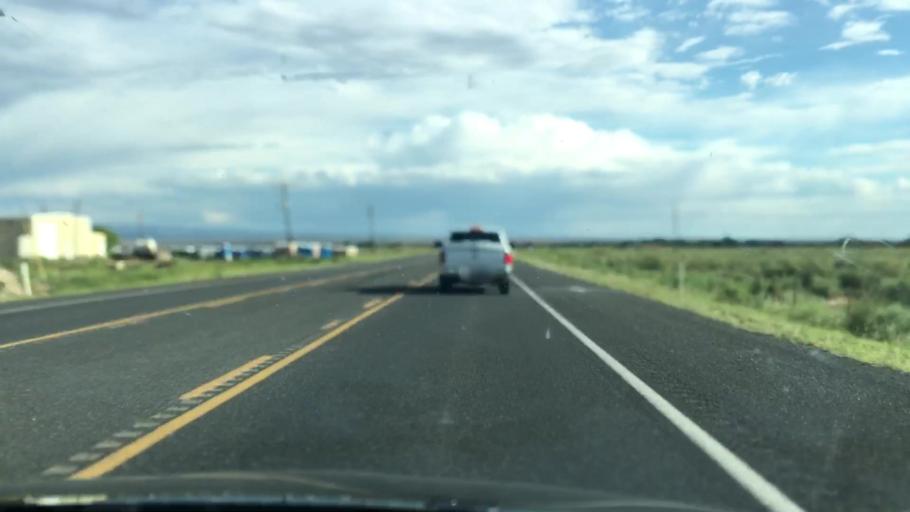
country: US
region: Arizona
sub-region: Coconino County
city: Fredonia
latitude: 36.9702
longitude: -112.5272
